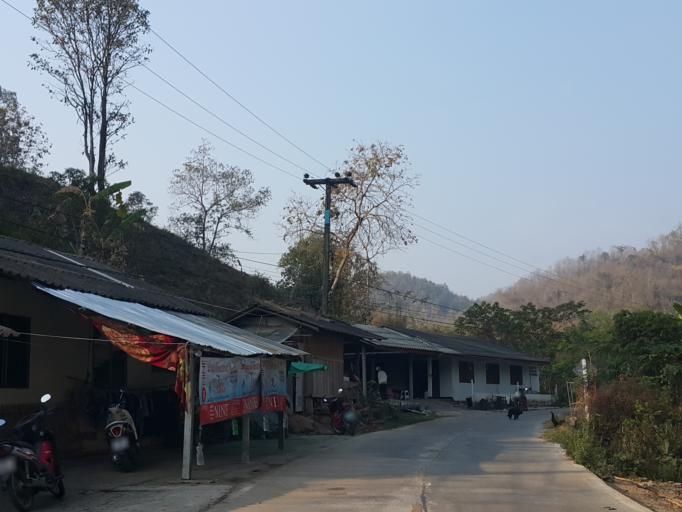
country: TH
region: Chiang Mai
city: Hang Dong
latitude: 18.7599
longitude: 98.8712
